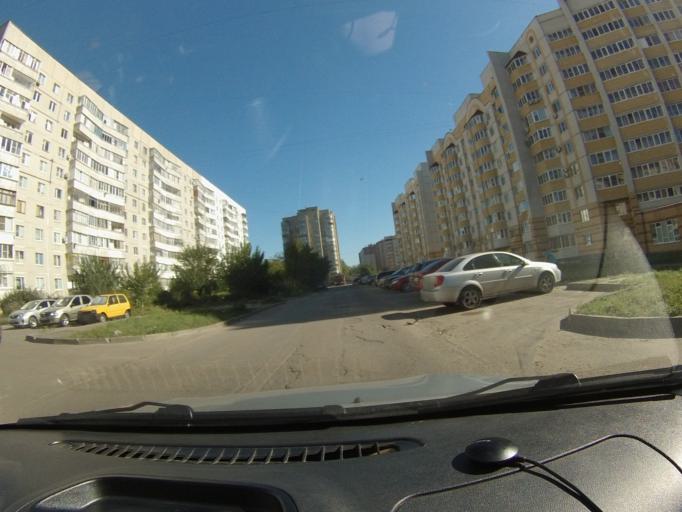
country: RU
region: Tambov
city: Tambov
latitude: 52.7660
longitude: 41.4012
